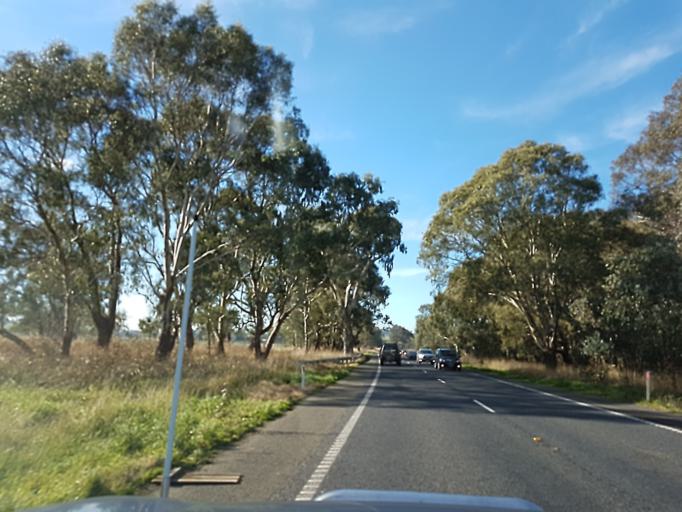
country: AU
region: Victoria
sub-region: Murrindindi
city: Alexandra
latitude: -37.1535
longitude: 145.5753
